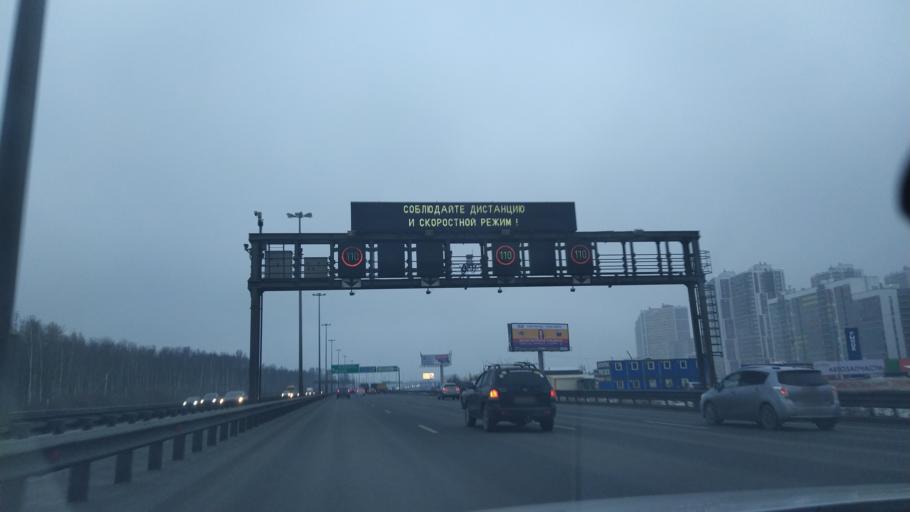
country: RU
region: Leningrad
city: Rybatskoye
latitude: 59.9066
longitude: 30.5262
